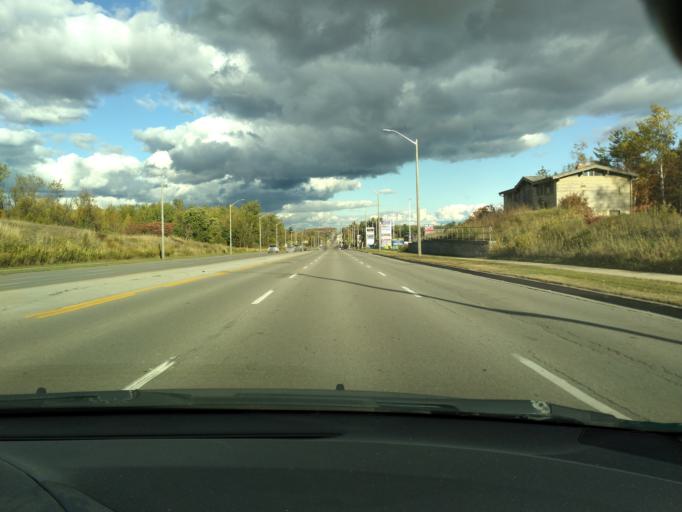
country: CA
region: Ontario
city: Innisfil
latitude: 44.3395
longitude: -79.6667
